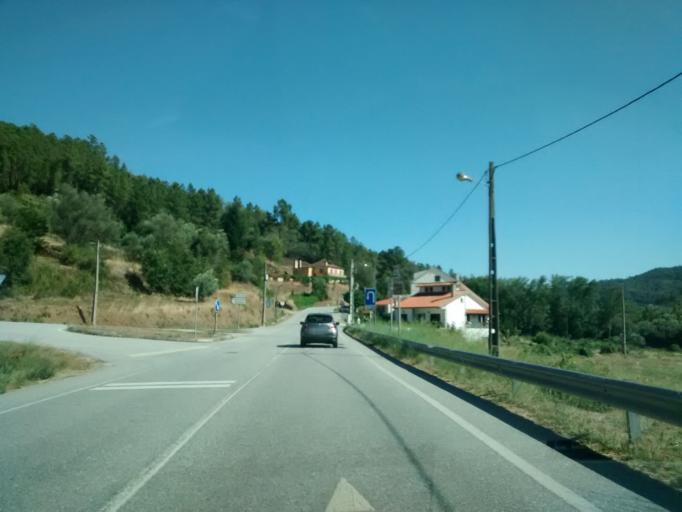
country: PT
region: Castelo Branco
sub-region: Belmonte
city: Belmonte
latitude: 40.4058
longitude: -7.3982
